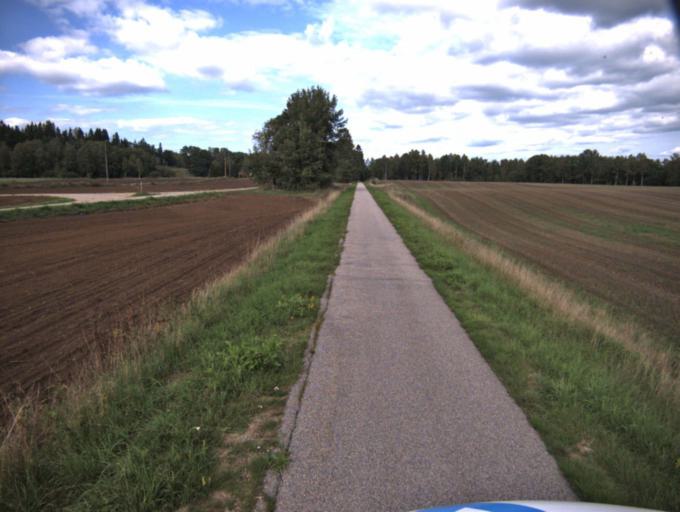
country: SE
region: Vaestra Goetaland
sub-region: Ulricehamns Kommun
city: Ulricehamn
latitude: 57.8411
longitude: 13.4212
